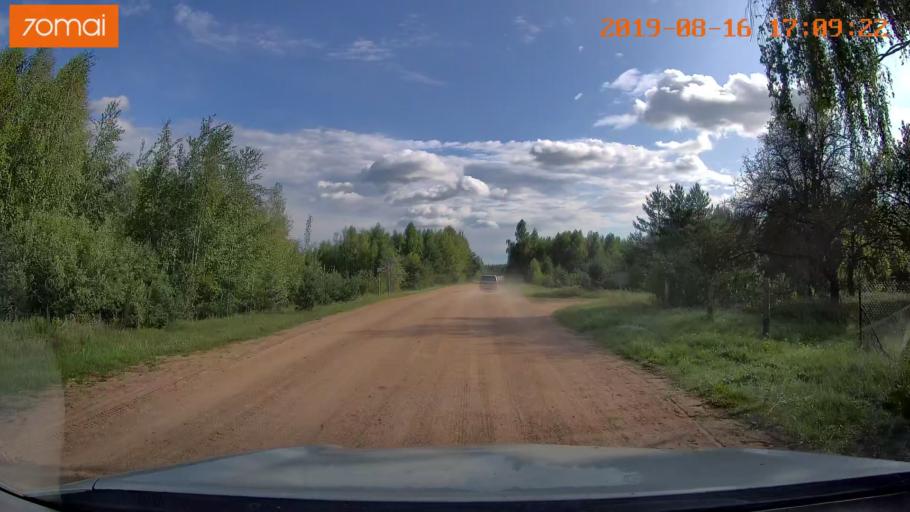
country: BY
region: Mogilev
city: Hlusha
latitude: 53.2139
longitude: 28.9249
